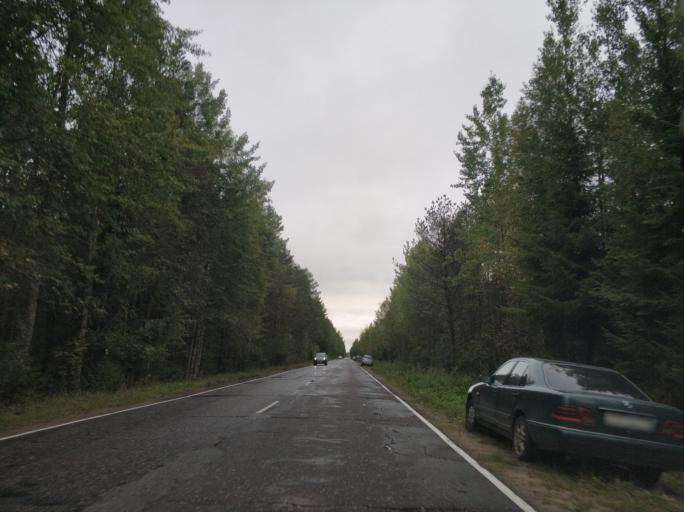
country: RU
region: Leningrad
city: Borisova Griva
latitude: 60.1694
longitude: 30.9203
